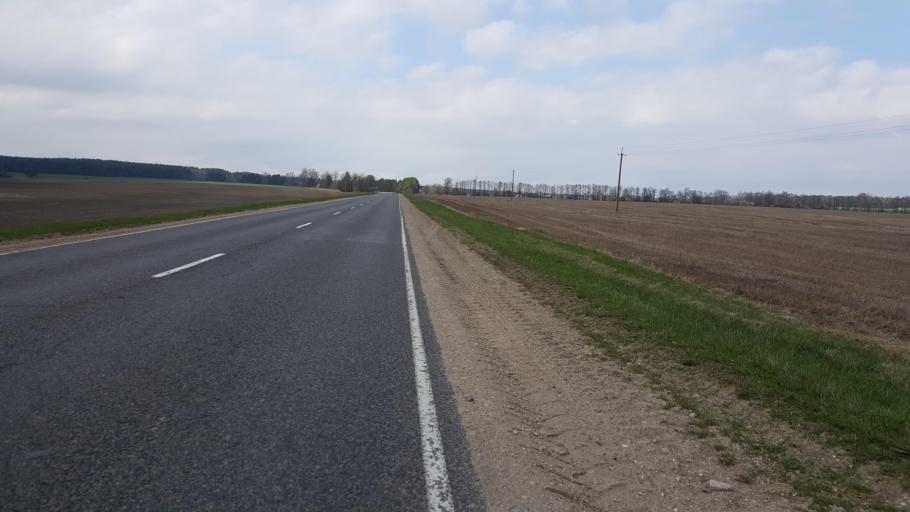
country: BY
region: Brest
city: Kamyanyets
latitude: 52.3655
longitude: 23.8878
